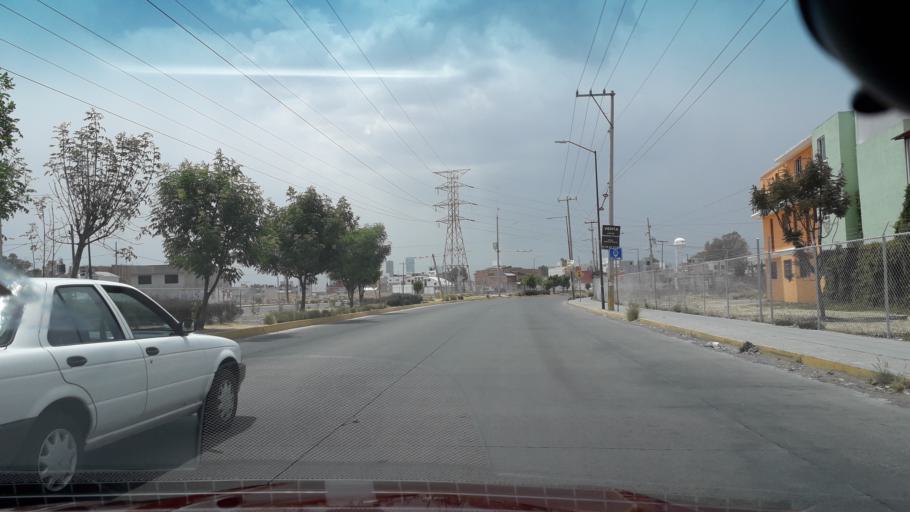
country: MX
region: Puebla
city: Tlazcalancingo
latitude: 19.0060
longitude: -98.2419
